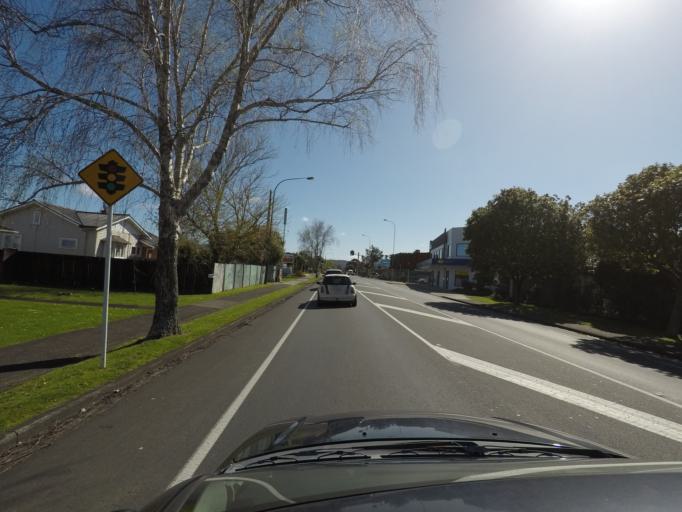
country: NZ
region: Auckland
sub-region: Auckland
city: Rosebank
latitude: -36.8638
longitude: 174.6033
